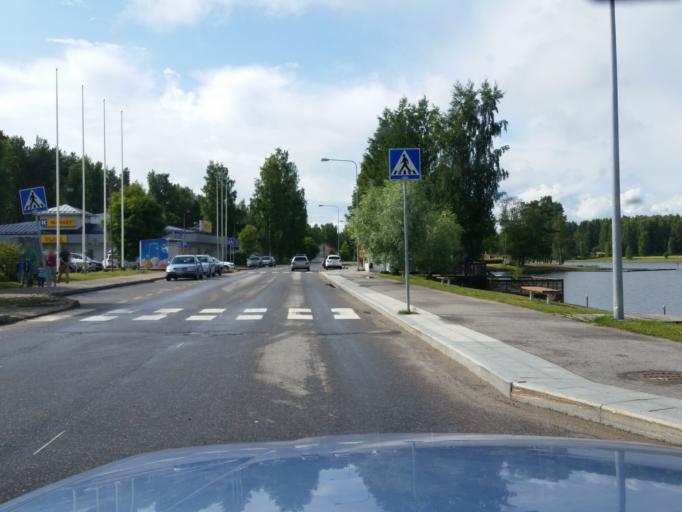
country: FI
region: Southern Savonia
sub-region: Savonlinna
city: Sulkava
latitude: 61.7872
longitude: 28.3720
